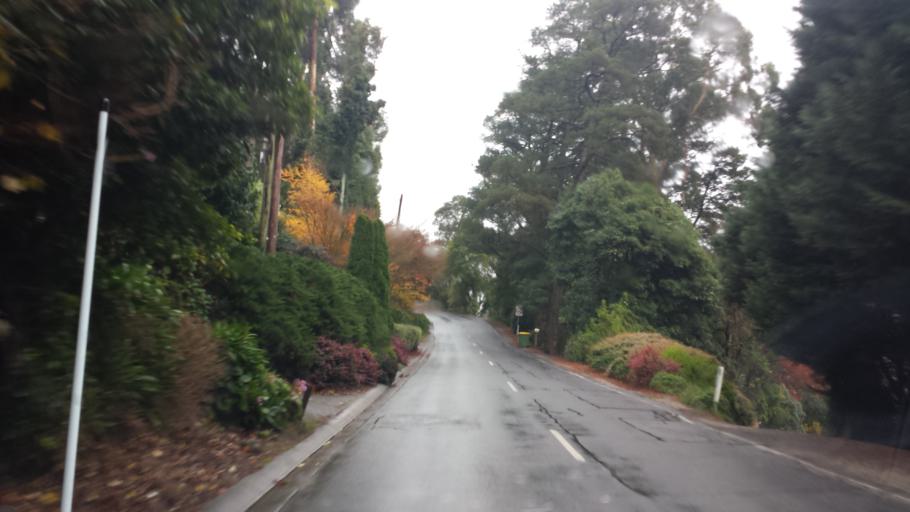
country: AU
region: Victoria
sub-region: Yarra Ranges
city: Monbulk
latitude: -37.8875
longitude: 145.3864
